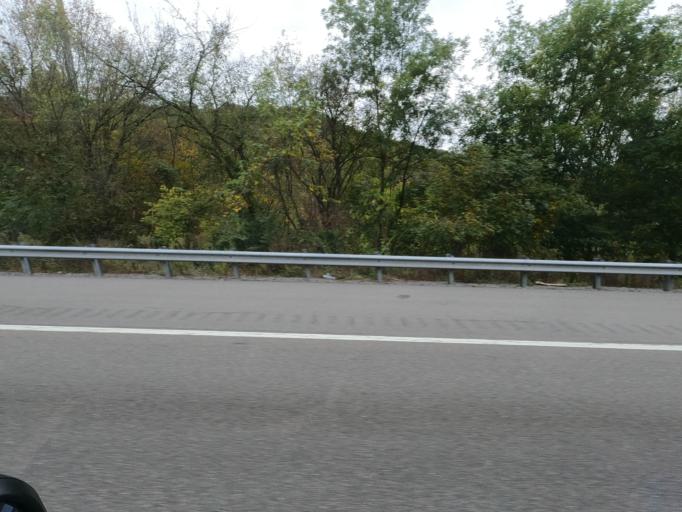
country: US
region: Tennessee
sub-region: Sullivan County
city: Colonial Heights
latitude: 36.4940
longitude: -82.5563
